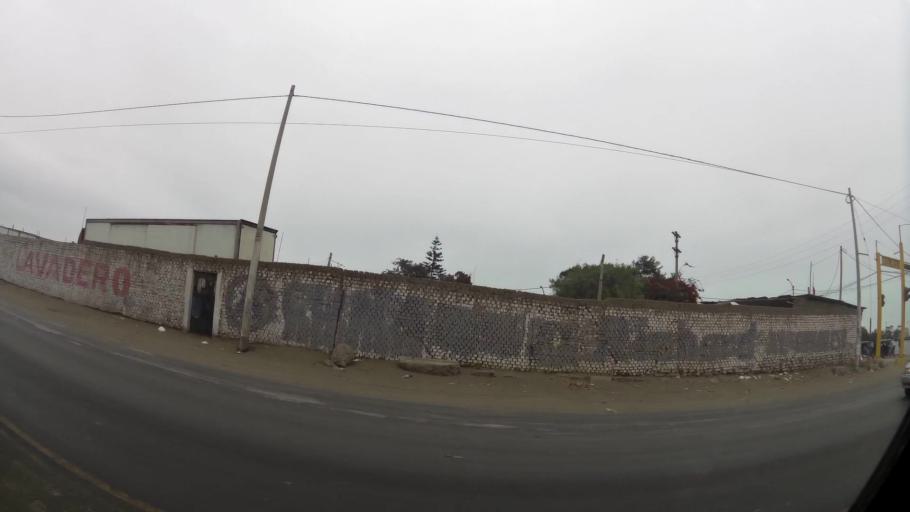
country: PE
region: La Libertad
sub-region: Provincia de Trujillo
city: Moche
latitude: -8.1680
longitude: -79.0060
